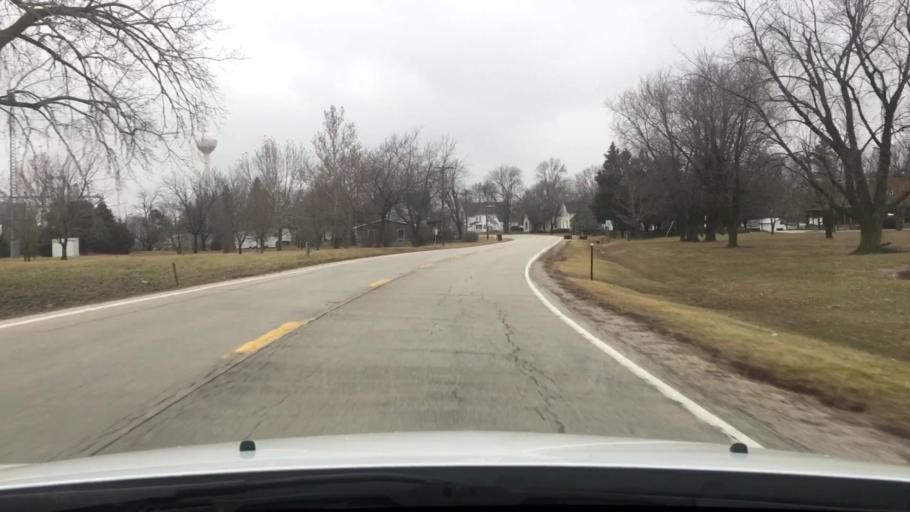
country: US
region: Illinois
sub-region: Iroquois County
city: Sheldon
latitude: 40.8797
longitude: -87.6150
